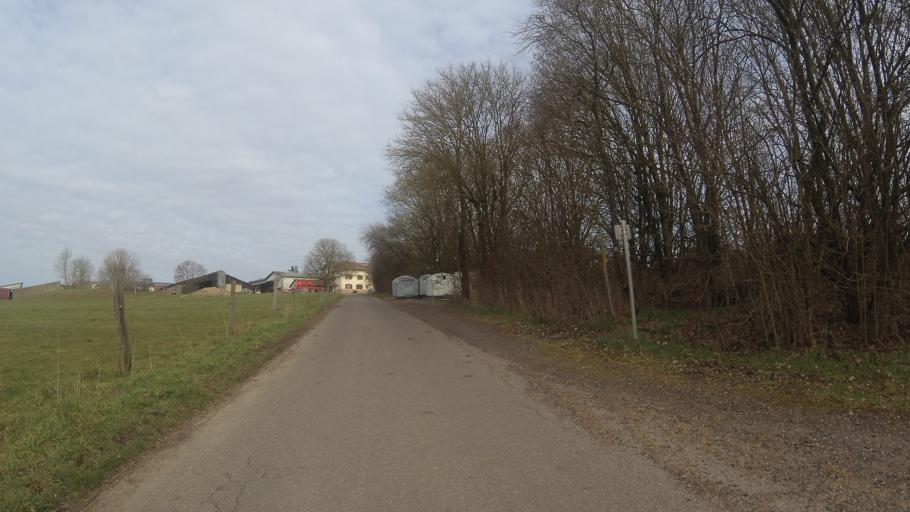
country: FR
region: Lorraine
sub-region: Departement de la Moselle
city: Merten
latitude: 49.3021
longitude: 6.6406
